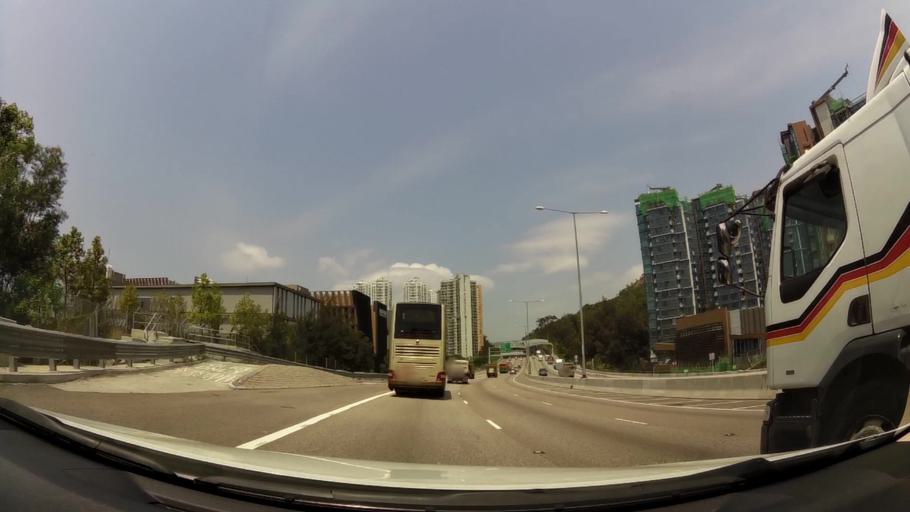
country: HK
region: Tuen Mun
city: Tuen Mun
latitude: 22.3756
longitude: 113.9881
